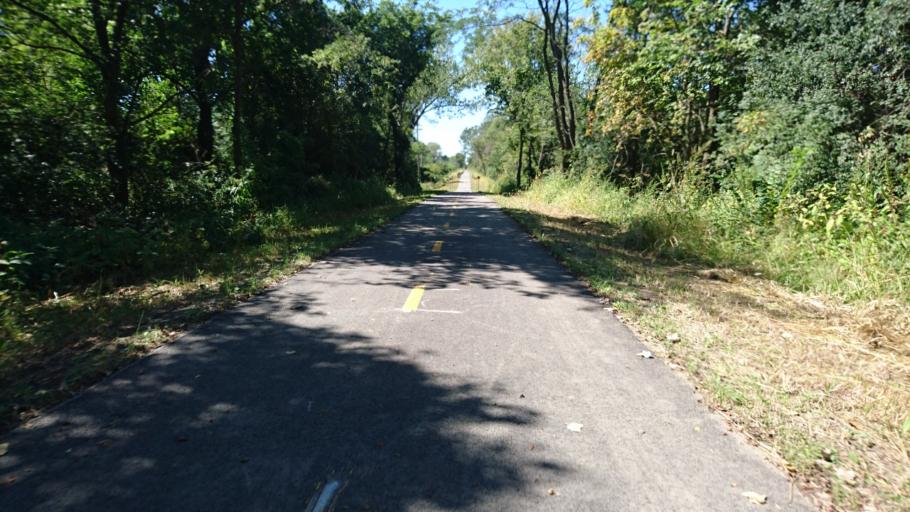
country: US
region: Illinois
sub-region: Cook County
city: Chicago Heights
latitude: 41.4991
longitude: -87.6535
